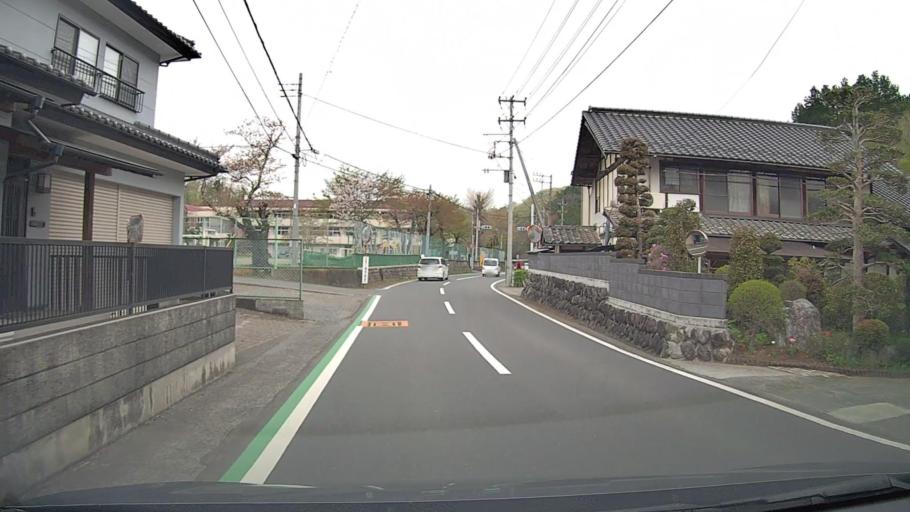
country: JP
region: Saitama
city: Chichibu
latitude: 36.0550
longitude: 139.1308
